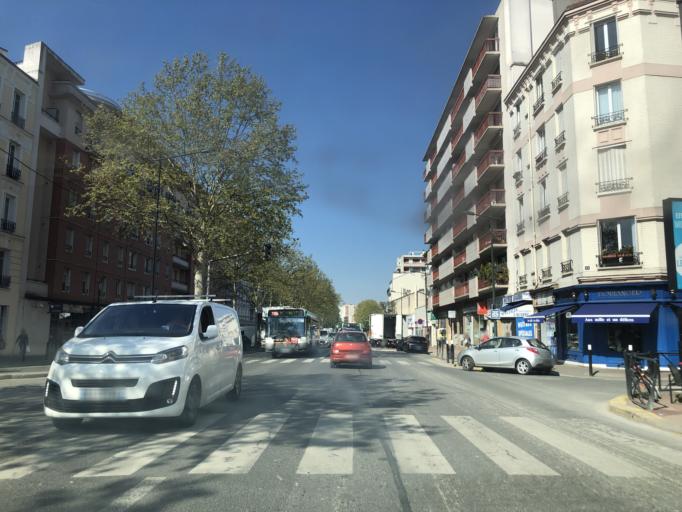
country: FR
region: Ile-de-France
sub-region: Departement du Val-de-Marne
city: Joinville-le-Pont
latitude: 48.8201
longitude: 2.4776
